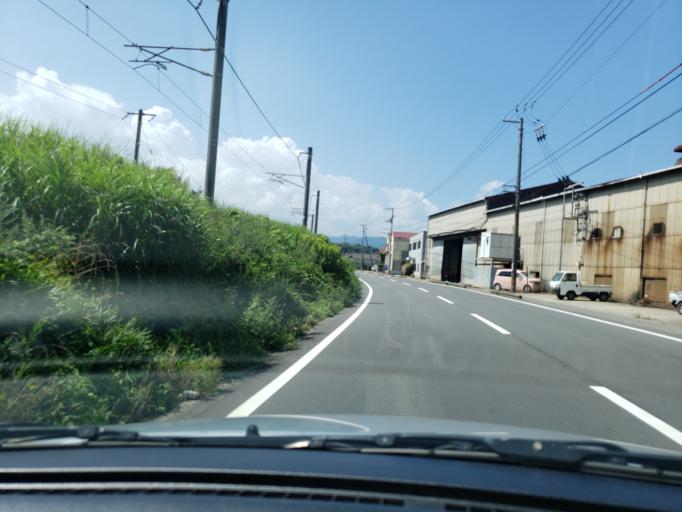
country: JP
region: Ehime
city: Hojo
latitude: 34.0918
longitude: 132.9328
